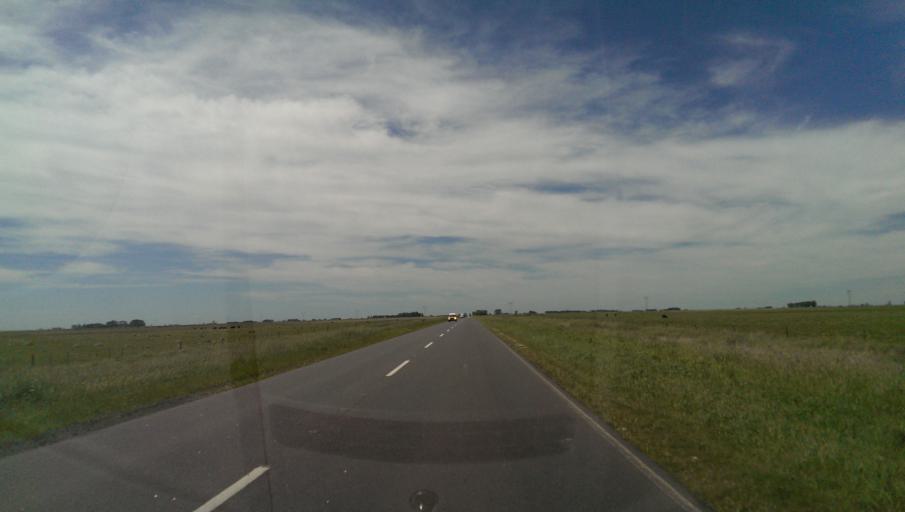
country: AR
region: Buenos Aires
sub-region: Partido de Laprida
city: Laprida
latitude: -37.2380
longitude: -60.7447
